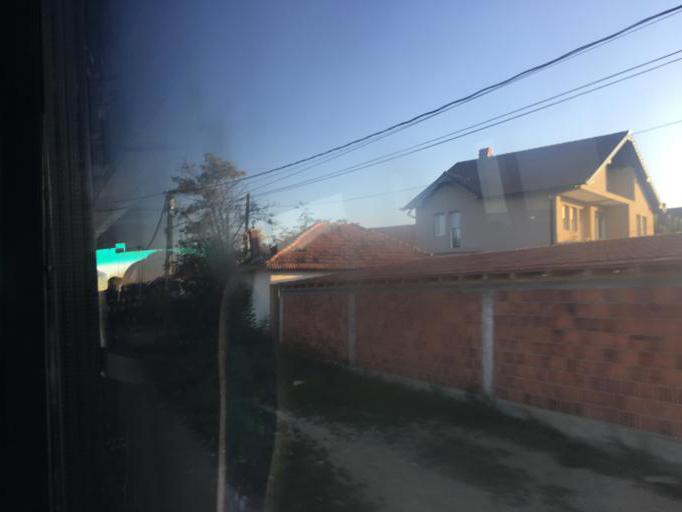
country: XK
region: Pristina
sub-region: Komuna e Drenasit
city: Glogovac
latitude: 42.5892
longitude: 20.8932
